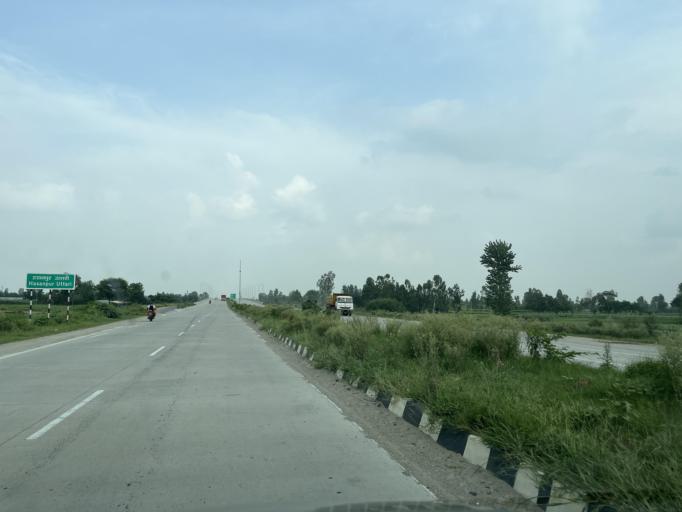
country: IN
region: Uttarakhand
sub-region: Udham Singh Nagar
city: Bazpur
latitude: 29.1483
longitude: 79.0508
